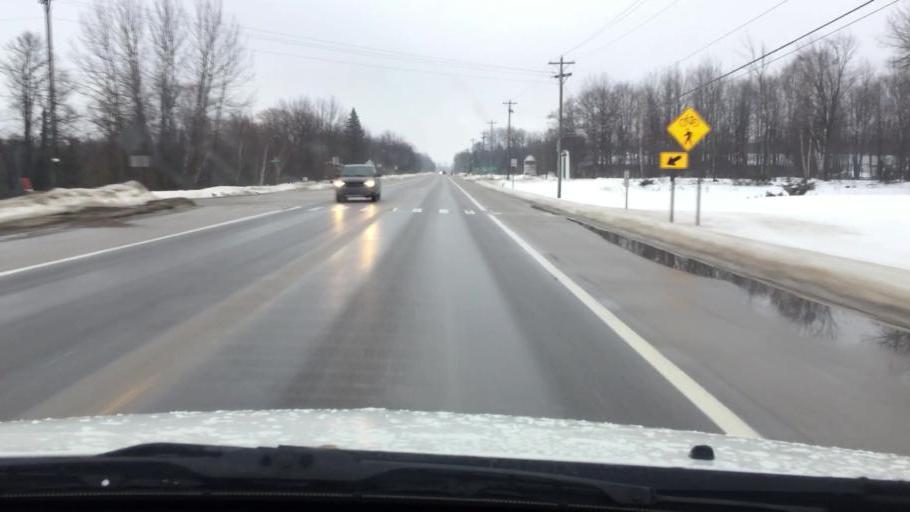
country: US
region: Michigan
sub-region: Charlevoix County
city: Charlevoix
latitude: 45.2945
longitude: -85.2524
